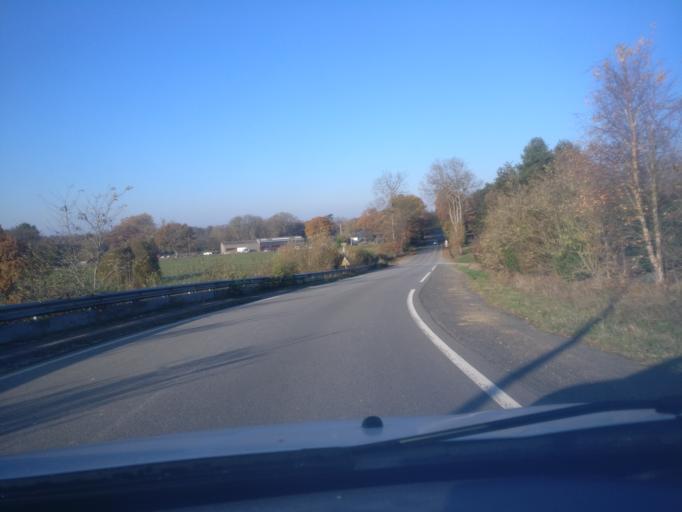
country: FR
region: Brittany
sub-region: Departement d'Ille-et-Vilaine
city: Bruz
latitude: 48.0276
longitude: -1.7693
